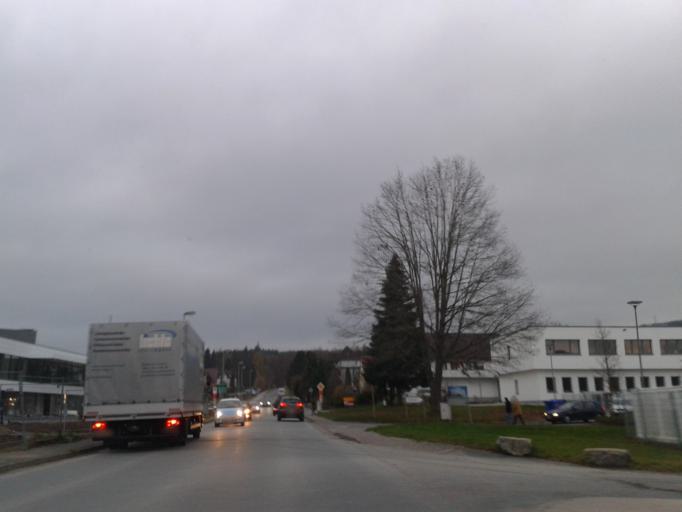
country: DE
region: North Rhine-Westphalia
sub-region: Regierungsbezirk Detmold
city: Blomberg
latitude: 51.9222
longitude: 9.1492
